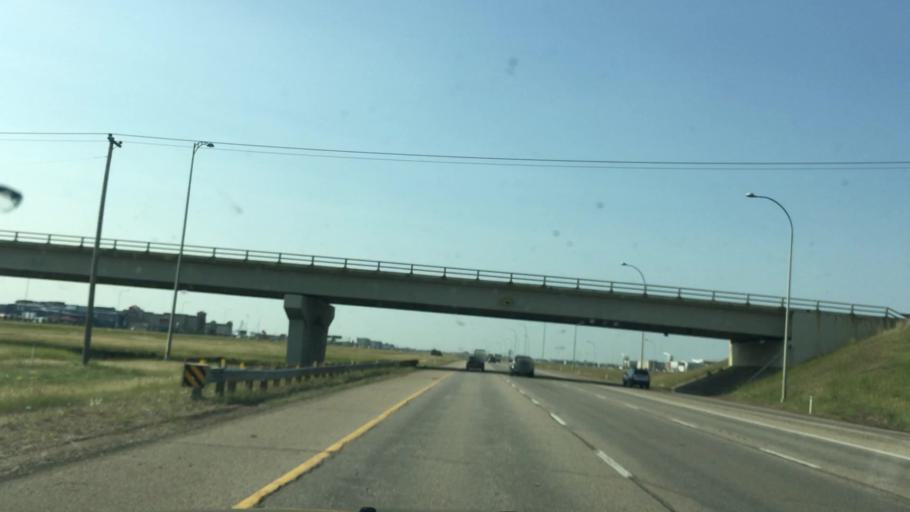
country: CA
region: Alberta
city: Leduc
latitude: 53.3095
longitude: -113.5499
